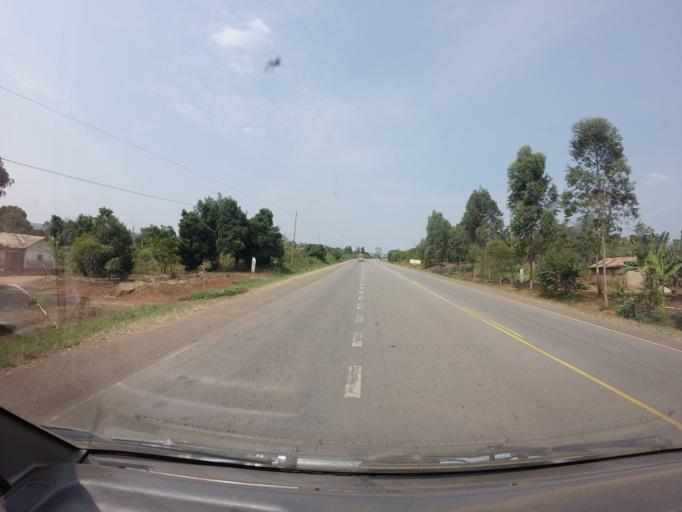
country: UG
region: Central Region
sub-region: Lwengo District
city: Lwengo
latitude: -0.3930
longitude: 31.3451
